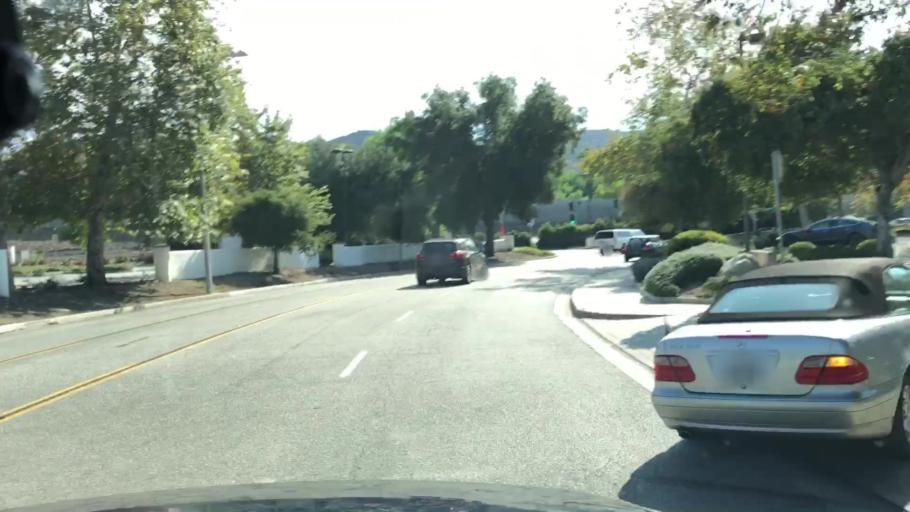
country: US
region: California
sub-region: Ventura County
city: Thousand Oaks
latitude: 34.1787
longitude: -118.8773
